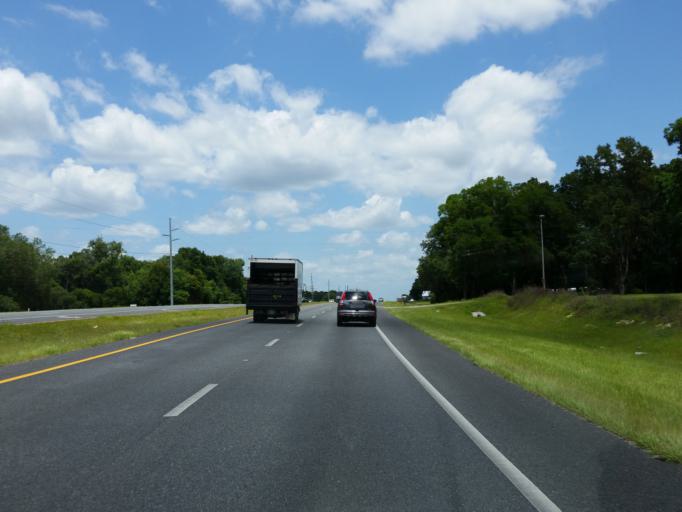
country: US
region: Florida
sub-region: Sumter County
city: The Villages
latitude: 28.9641
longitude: -82.0410
